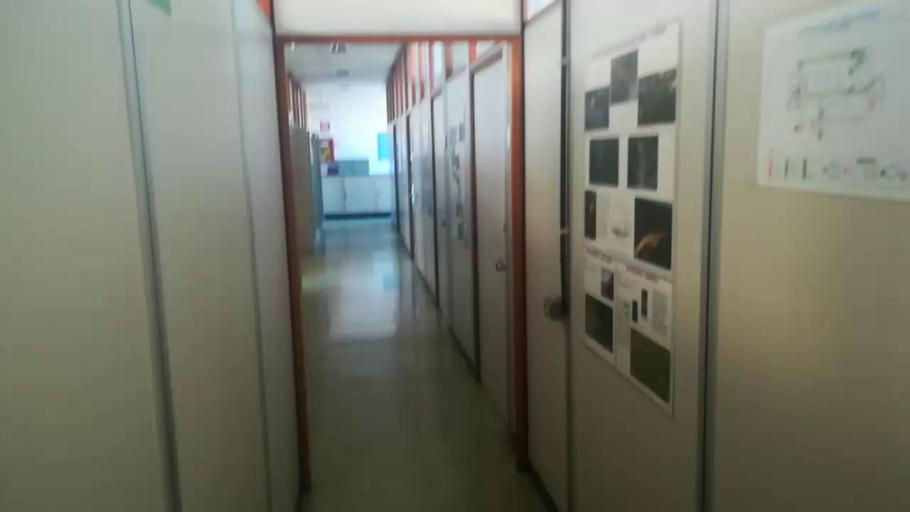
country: IT
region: Latium
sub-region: Citta metropolitana di Roma Capitale
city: Rome
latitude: 41.8932
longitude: 12.4936
